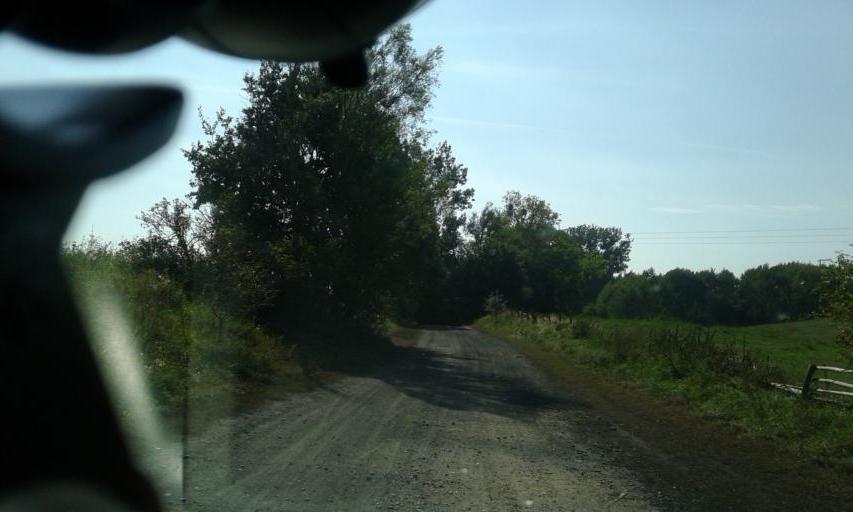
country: PL
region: West Pomeranian Voivodeship
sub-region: Powiat choszczenski
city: Krzecin
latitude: 53.0781
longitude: 15.5564
